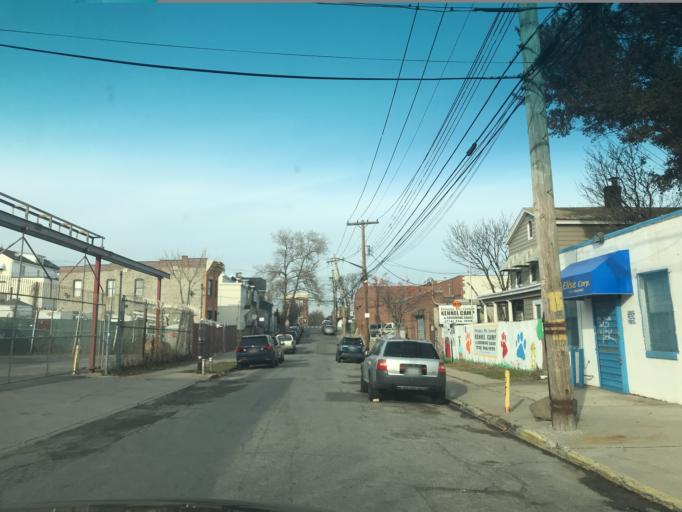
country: US
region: New York
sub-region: Bronx
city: The Bronx
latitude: 40.7837
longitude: -73.8404
